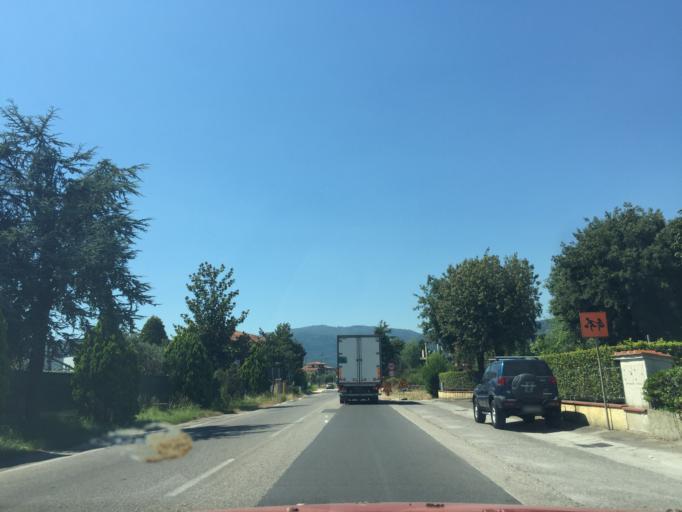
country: IT
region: Tuscany
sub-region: Provincia di Pistoia
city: Santa Lucia
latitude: 43.8722
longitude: 10.6941
